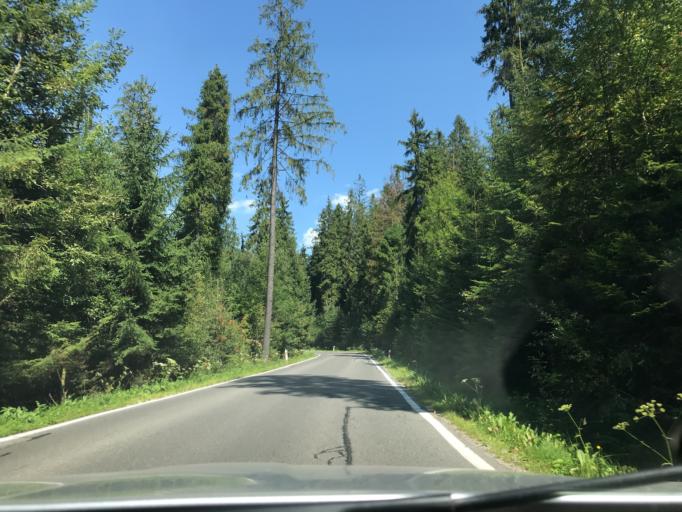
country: PL
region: Lesser Poland Voivodeship
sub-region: Powiat nowotarski
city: Klikuszowa
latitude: 49.5241
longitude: 19.9597
